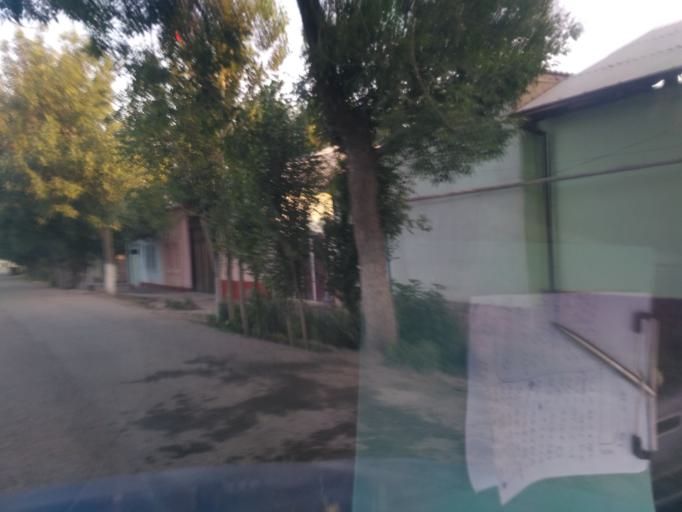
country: UZ
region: Sirdaryo
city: Guliston
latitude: 40.5006
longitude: 68.7697
